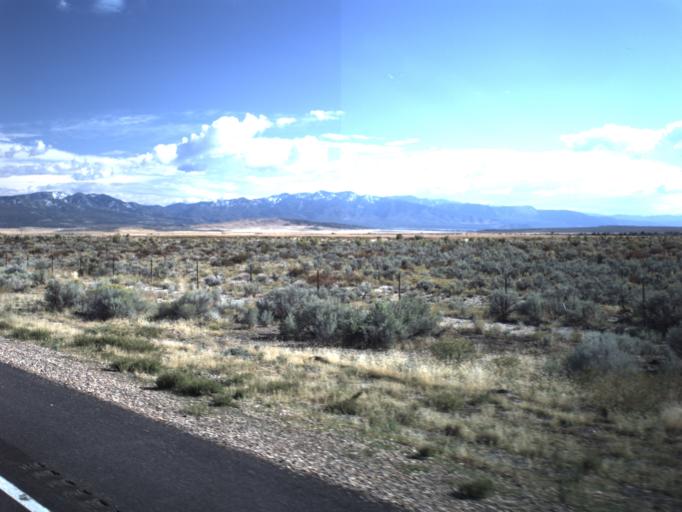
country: US
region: Utah
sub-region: Millard County
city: Fillmore
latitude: 39.1478
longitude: -112.3911
